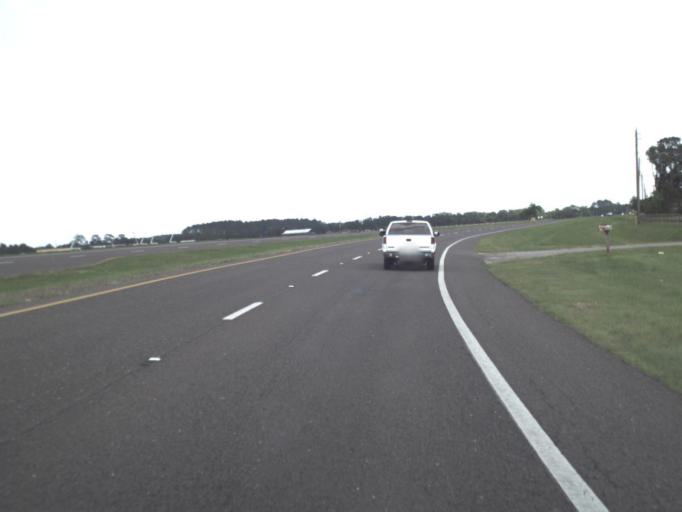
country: US
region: Florida
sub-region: Saint Johns County
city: Saint Augustine Shores
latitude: 29.7764
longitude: -81.4493
